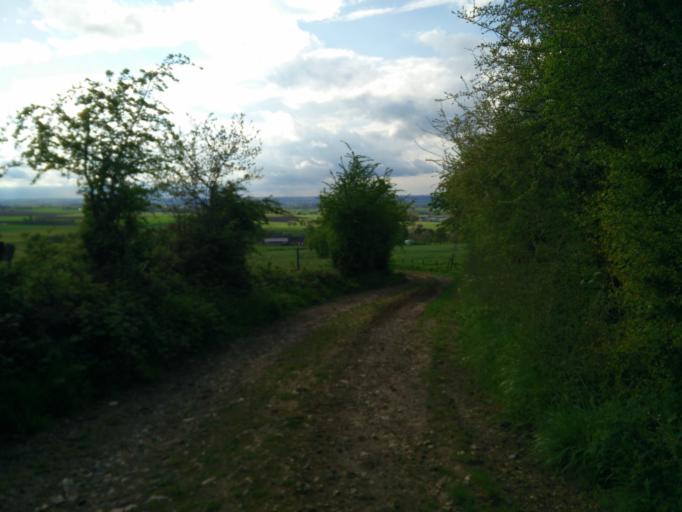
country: BE
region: Flanders
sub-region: Provincie Limburg
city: Sint-Pieters-Voeren
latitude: 50.7246
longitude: 5.7804
